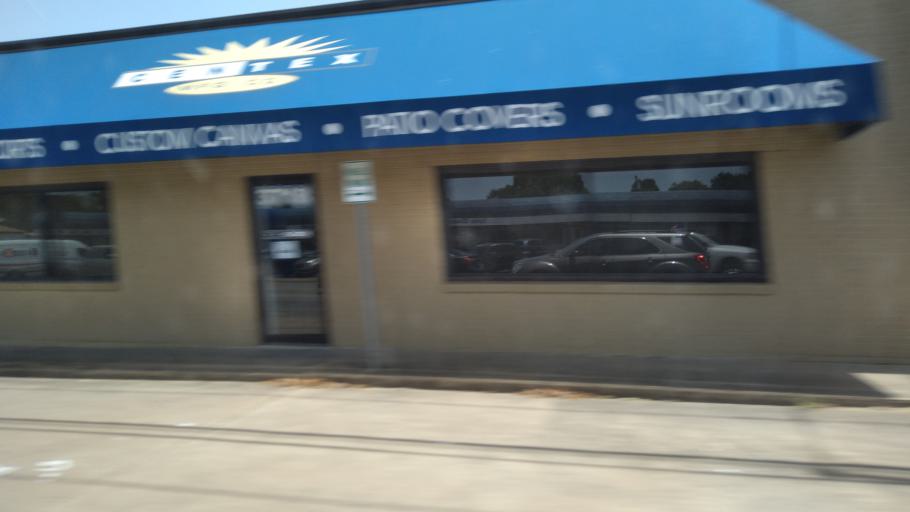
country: US
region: Texas
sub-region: McLennan County
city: Beverly Hills
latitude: 31.5297
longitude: -97.1606
